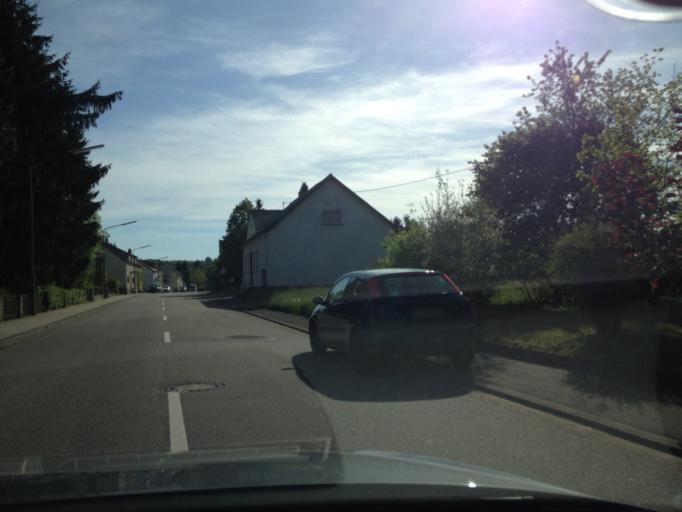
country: DE
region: Saarland
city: Bexbach
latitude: 49.3226
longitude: 7.2420
